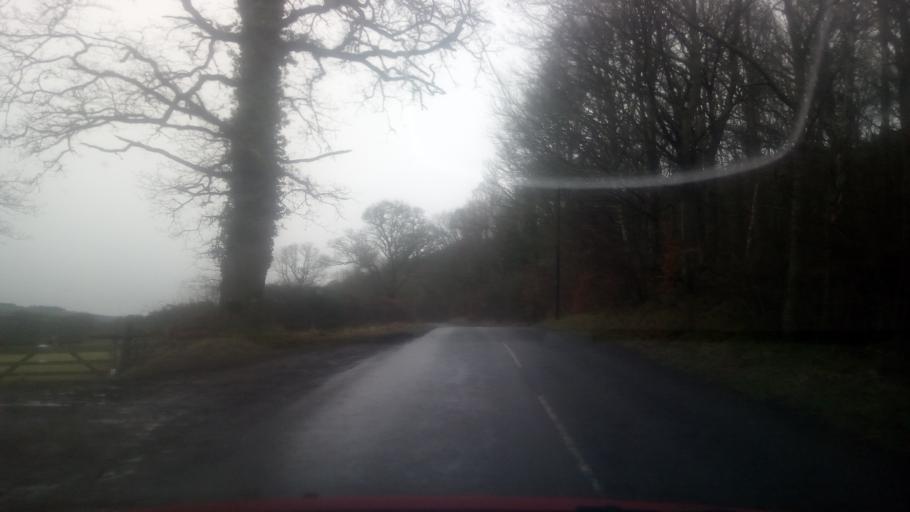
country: GB
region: Scotland
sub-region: The Scottish Borders
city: Earlston
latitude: 55.6191
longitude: -2.6645
